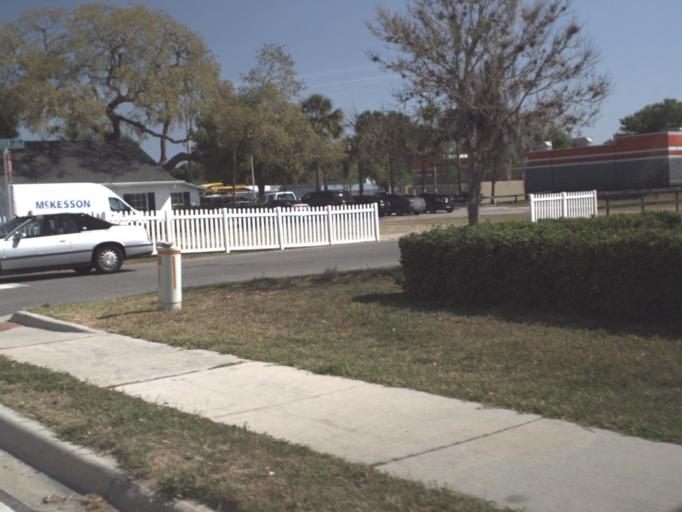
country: US
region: Florida
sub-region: Lake County
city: Leesburg
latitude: 28.8234
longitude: -81.8874
